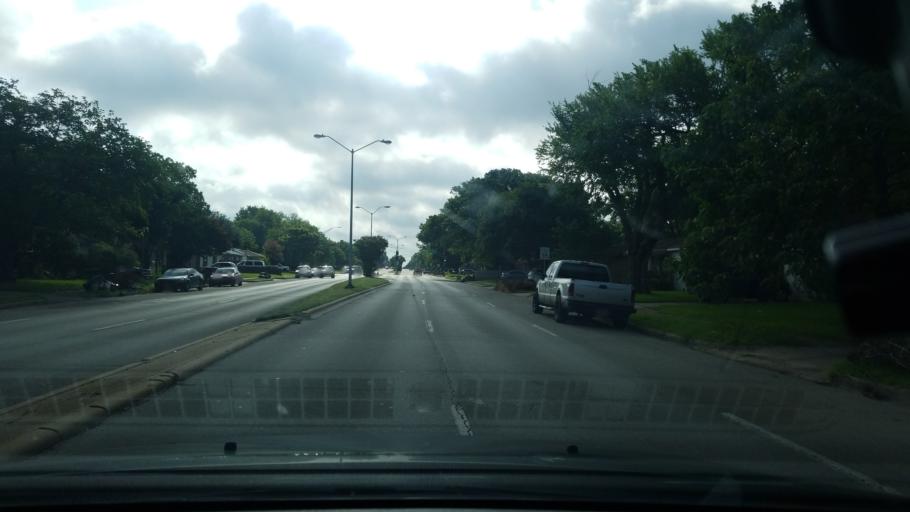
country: US
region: Texas
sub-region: Dallas County
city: Mesquite
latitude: 32.8215
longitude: -96.6698
